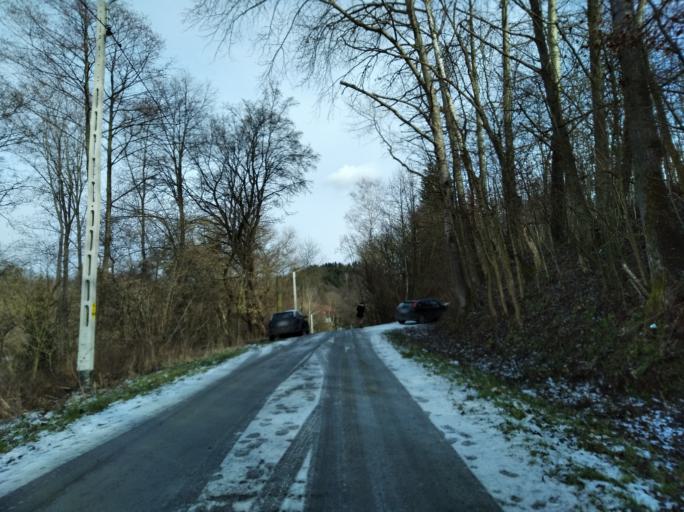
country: PL
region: Subcarpathian Voivodeship
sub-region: Powiat strzyzowski
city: Strzyzow
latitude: 49.9042
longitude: 21.7551
